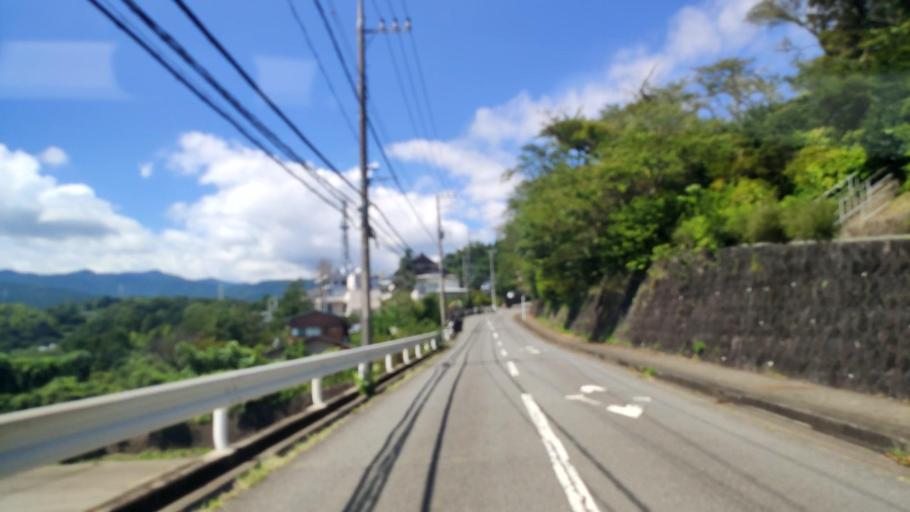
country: JP
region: Kanagawa
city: Odawara
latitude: 35.2518
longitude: 139.1417
